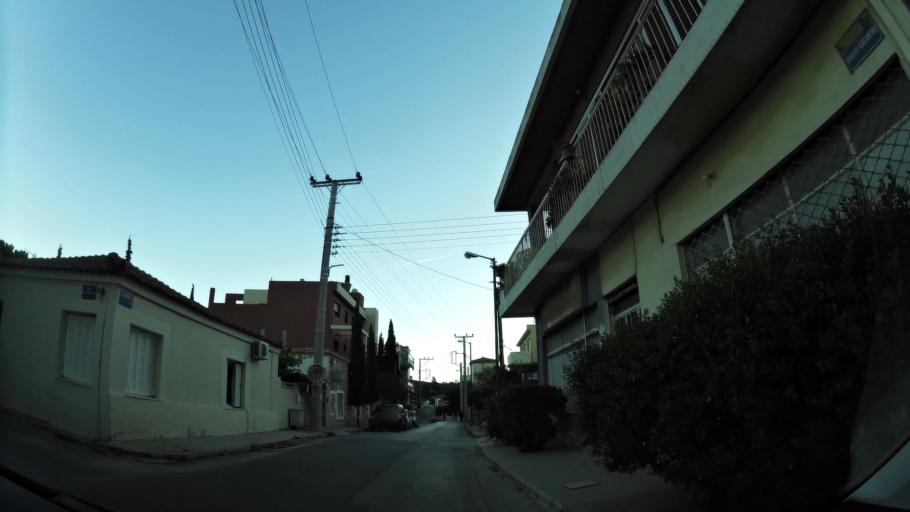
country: GR
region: Attica
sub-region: Nomarchia Anatolikis Attikis
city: Paiania
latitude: 37.9559
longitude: 23.8495
